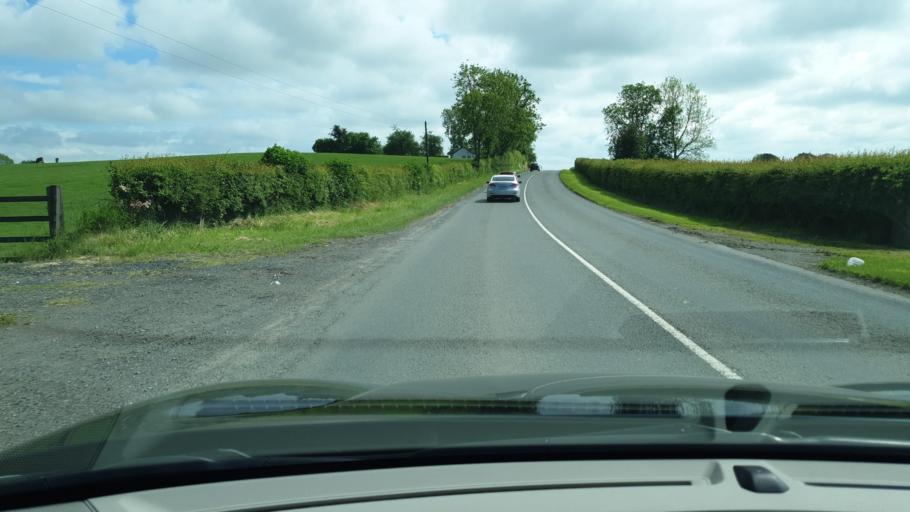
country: IE
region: Ulster
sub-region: An Cabhan
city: Kingscourt
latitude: 53.8105
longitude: -6.7374
